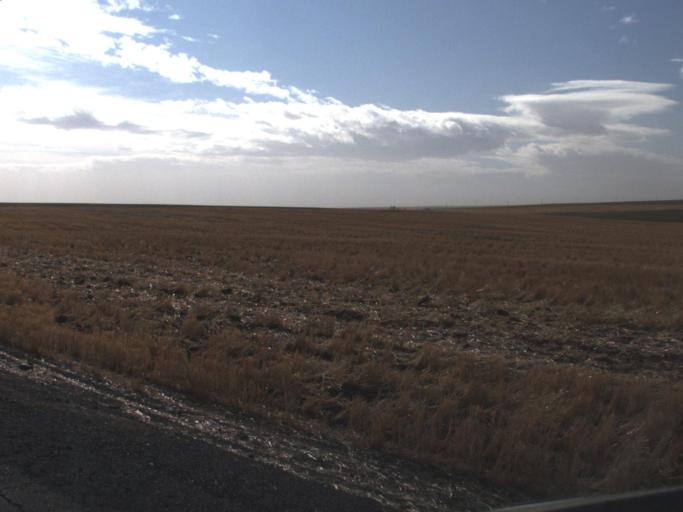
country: US
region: Washington
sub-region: Okanogan County
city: Coulee Dam
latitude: 47.6361
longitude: -118.7209
